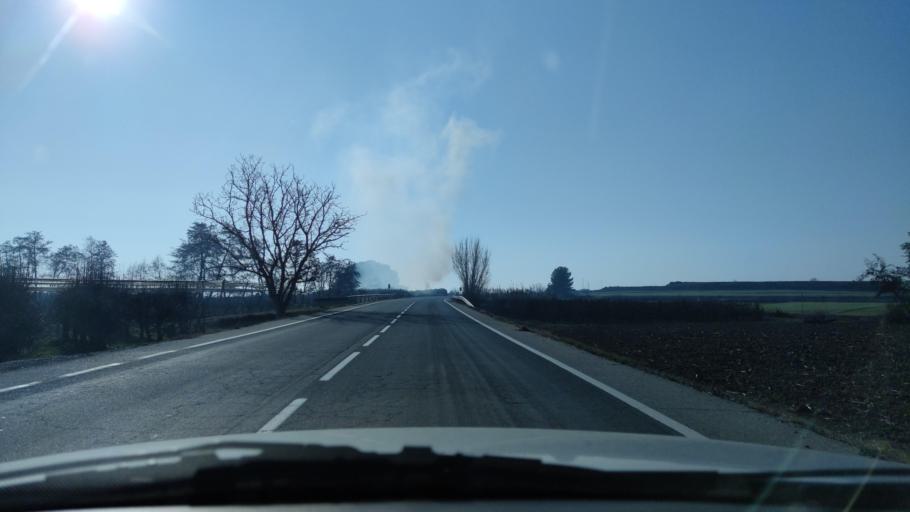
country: ES
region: Catalonia
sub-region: Provincia de Lleida
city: Albesa
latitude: 41.7247
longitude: 0.6403
